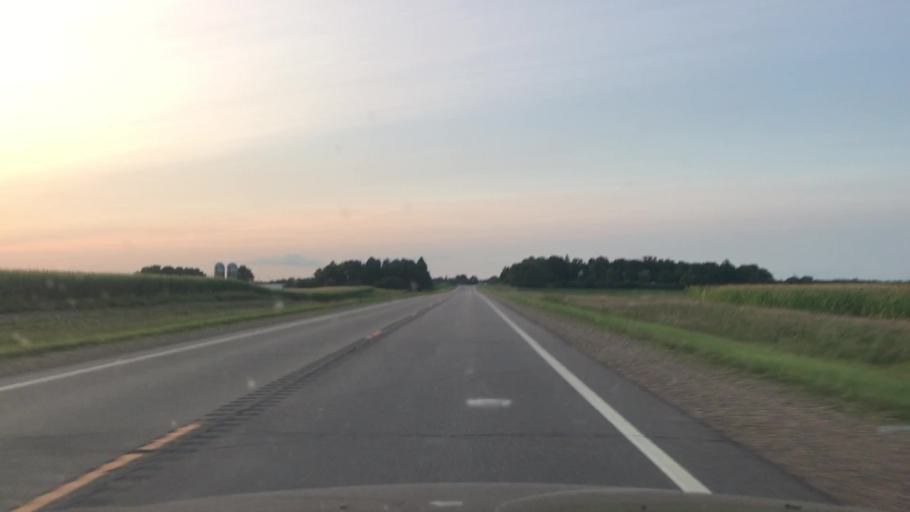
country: US
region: Minnesota
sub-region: Redwood County
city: Redwood Falls
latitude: 44.5134
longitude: -95.1181
